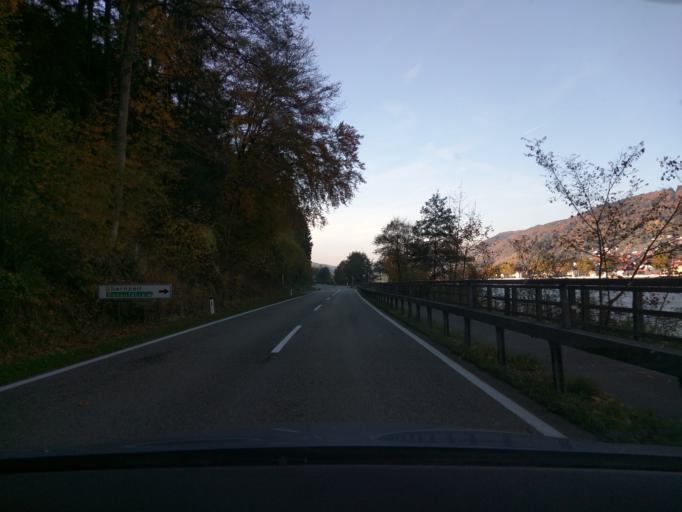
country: DE
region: Bavaria
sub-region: Lower Bavaria
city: Obernzell
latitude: 48.5503
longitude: 13.6428
